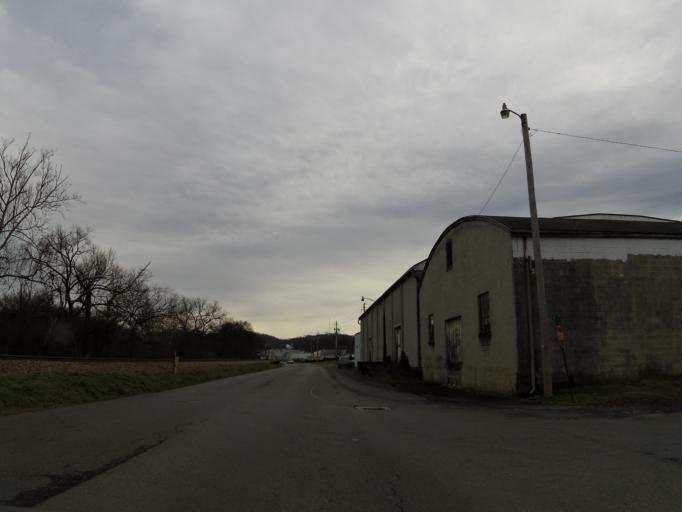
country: US
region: Tennessee
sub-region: Cocke County
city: Newport
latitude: 35.9685
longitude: -83.1933
